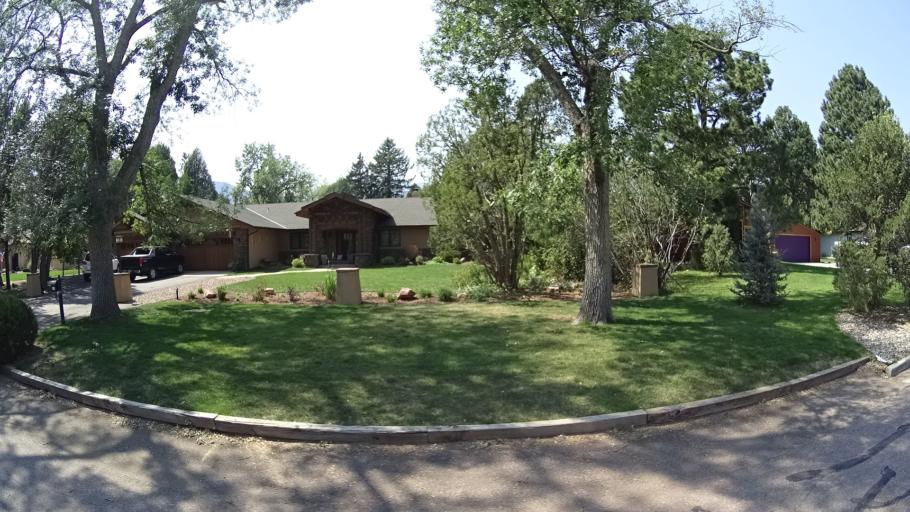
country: US
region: Colorado
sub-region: El Paso County
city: Colorado Springs
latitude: 38.7953
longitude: -104.8466
